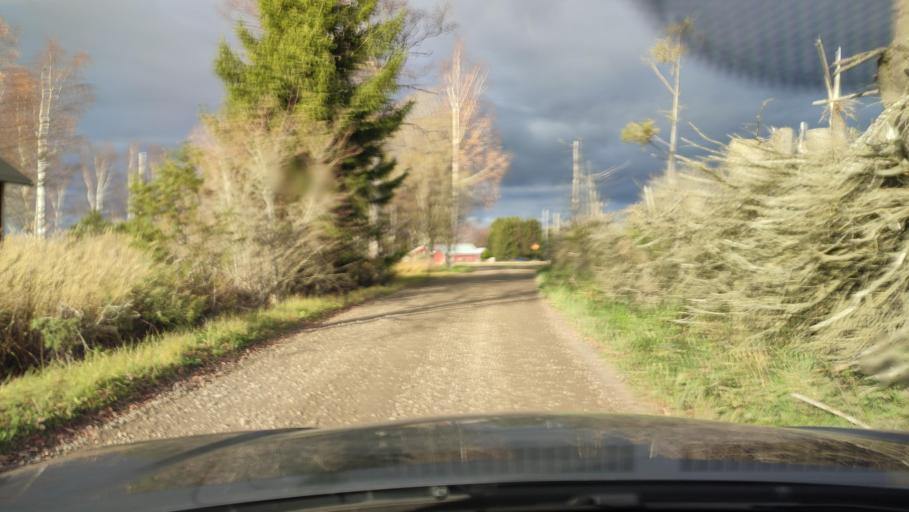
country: FI
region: Southern Ostrobothnia
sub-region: Suupohja
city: Karijoki
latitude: 62.2359
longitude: 21.5702
